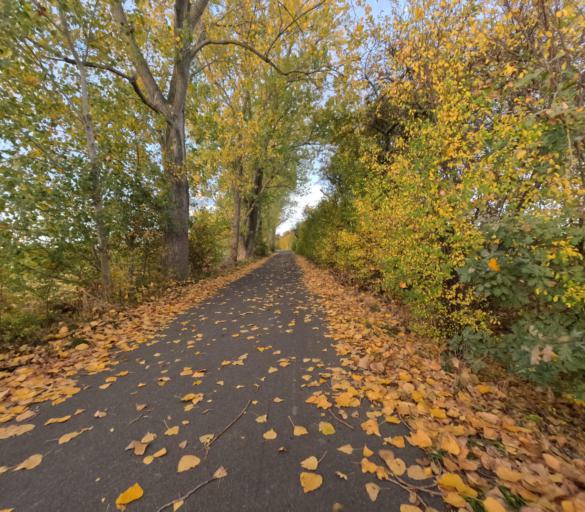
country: DE
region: Saxony
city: Grimma
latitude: 51.2460
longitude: 12.6942
